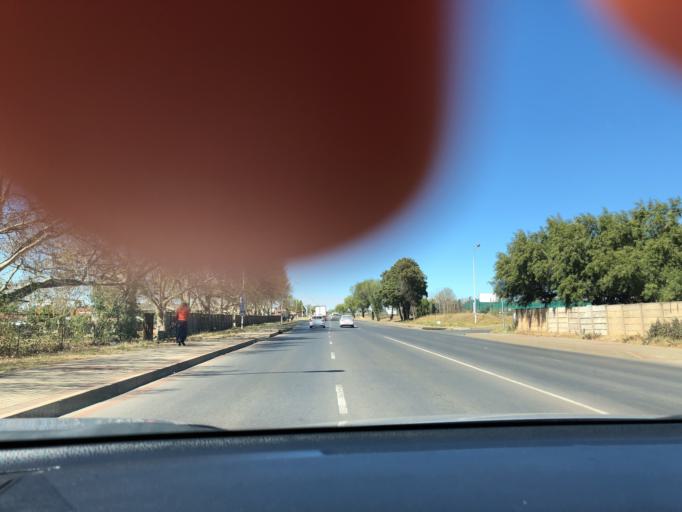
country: ZA
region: KwaZulu-Natal
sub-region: Amajuba District Municipality
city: Newcastle
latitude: -27.7563
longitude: 29.9420
